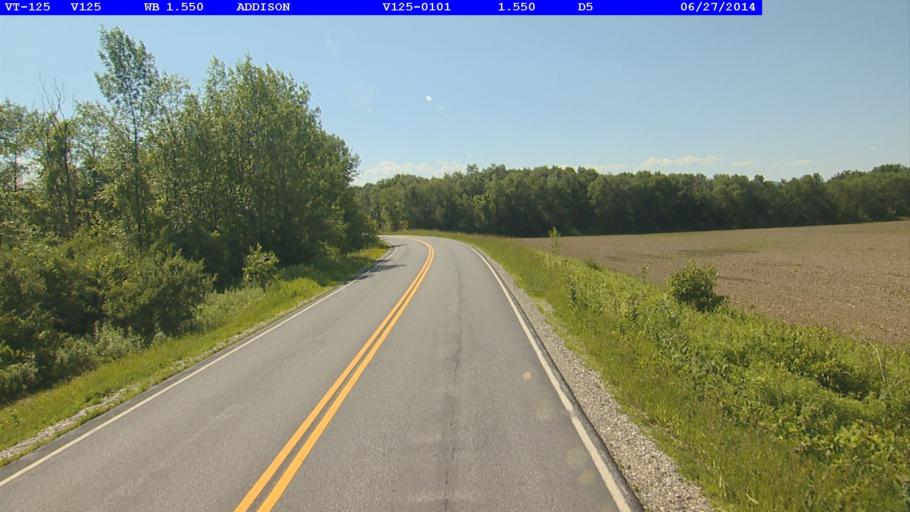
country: US
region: New York
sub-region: Essex County
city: Port Henry
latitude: 44.0249
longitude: -73.3943
